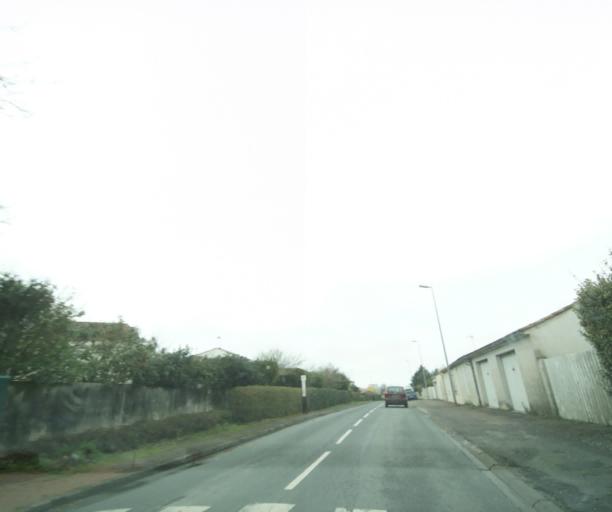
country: FR
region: Poitou-Charentes
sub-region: Departement de la Charente-Maritime
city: Puilboreau
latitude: 46.1723
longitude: -1.1244
